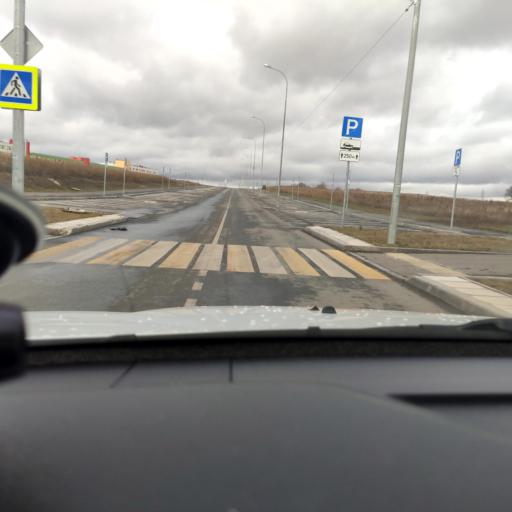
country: RU
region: Samara
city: Petra-Dubrava
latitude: 53.3034
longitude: 50.3294
